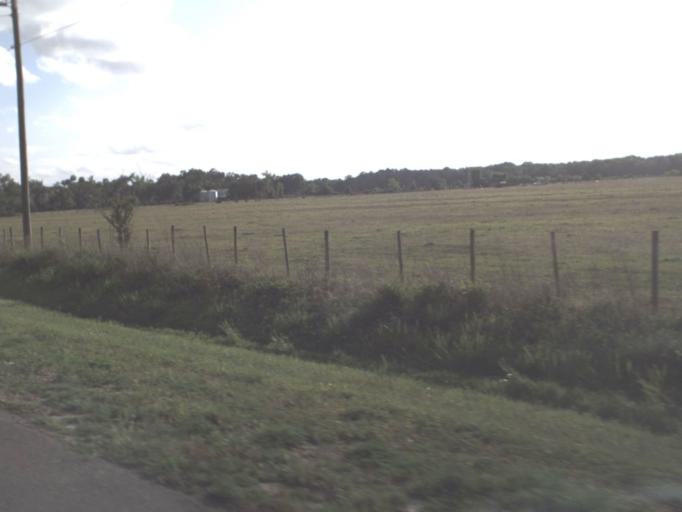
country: US
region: Florida
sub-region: Flagler County
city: Bunnell
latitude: 29.3195
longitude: -81.3105
